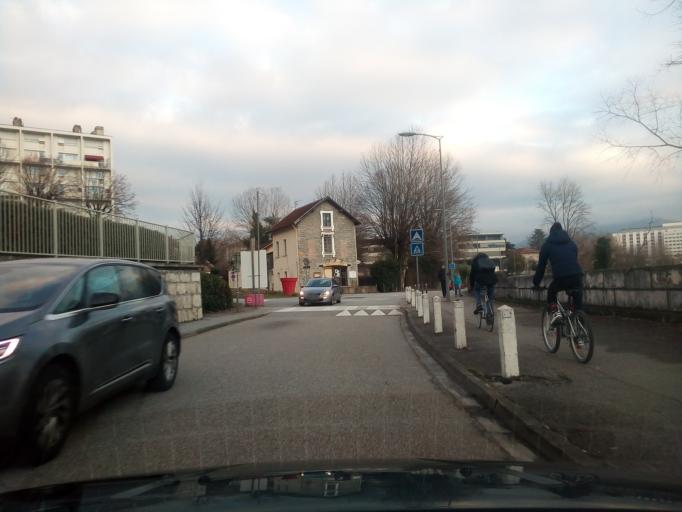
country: FR
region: Rhone-Alpes
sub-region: Departement de l'Isere
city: La Tronche
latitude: 45.2026
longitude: 5.7374
